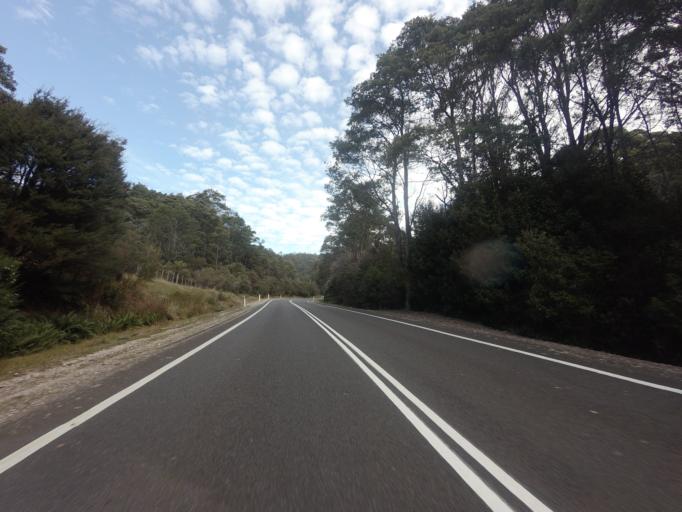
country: AU
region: Tasmania
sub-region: Meander Valley
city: Deloraine
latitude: -41.6507
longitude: 146.7173
